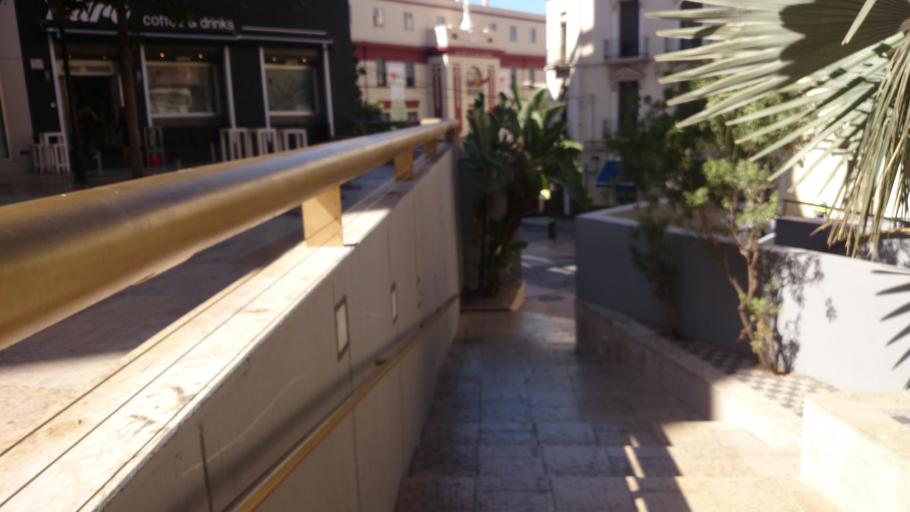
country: ES
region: Ceuta
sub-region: Ceuta
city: Ceuta
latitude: 35.8877
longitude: -5.3104
